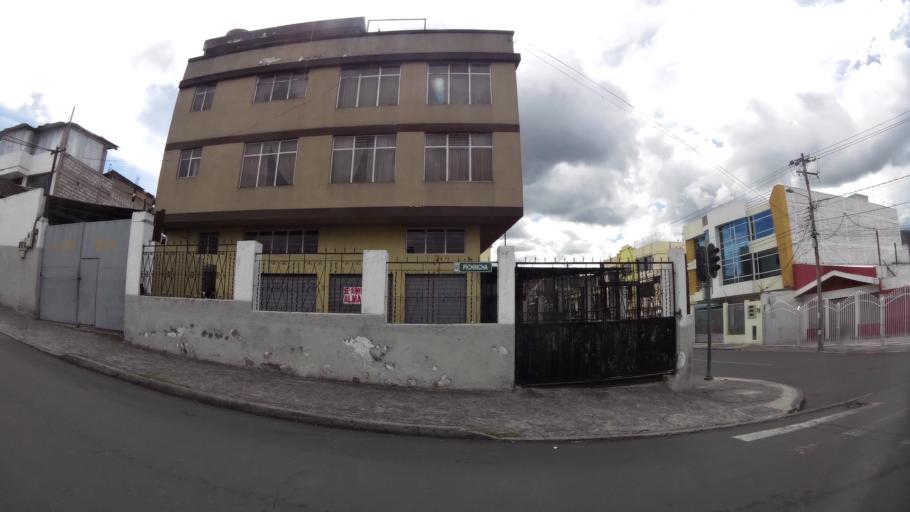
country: EC
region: Tungurahua
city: Ambato
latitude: -1.2485
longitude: -78.6258
